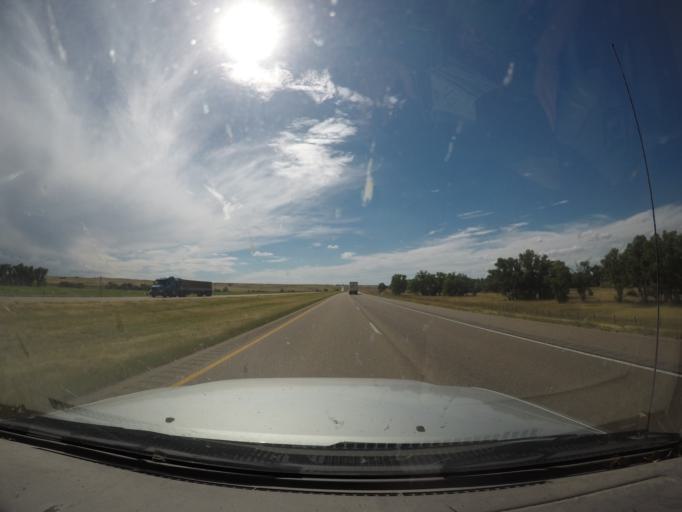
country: US
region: Nebraska
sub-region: Deuel County
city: Chappell
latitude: 41.0561
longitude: -102.4218
